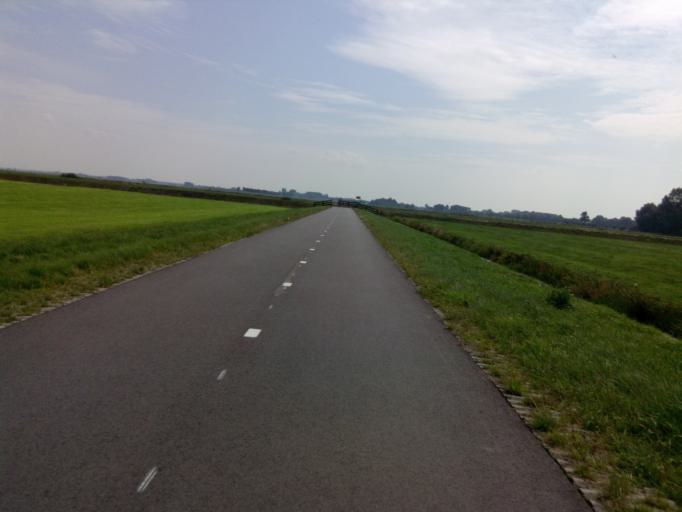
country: NL
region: Utrecht
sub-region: Gemeente Bunschoten
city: Bunschoten
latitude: 52.2286
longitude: 5.3942
